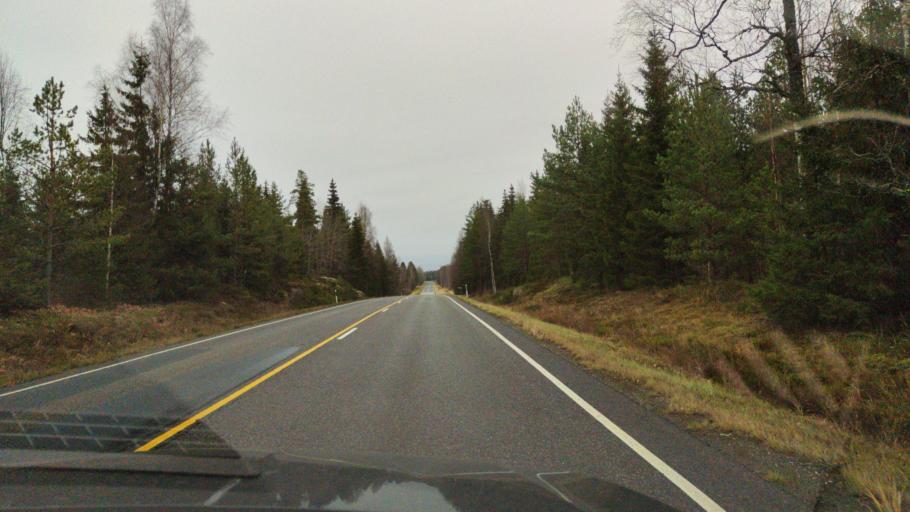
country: FI
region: Varsinais-Suomi
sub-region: Loimaa
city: Ylaene
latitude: 60.7716
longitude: 22.4387
